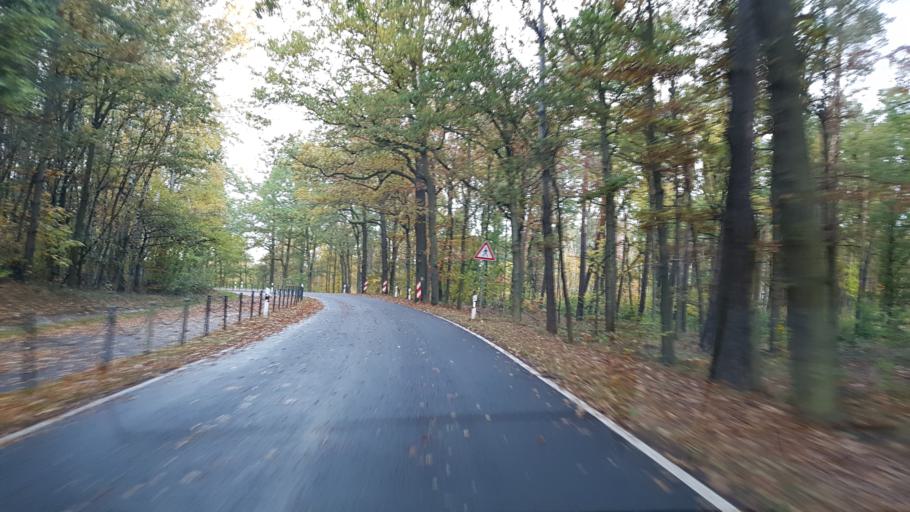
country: DE
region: Saxony
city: Dahlen
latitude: 51.3958
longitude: 13.0020
